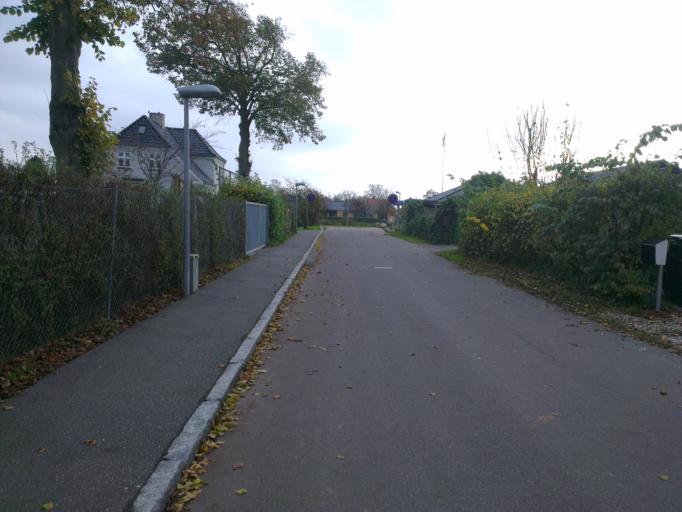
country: DK
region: Capital Region
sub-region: Frederikssund Kommune
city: Jaegerspris
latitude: 55.8548
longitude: 11.9864
